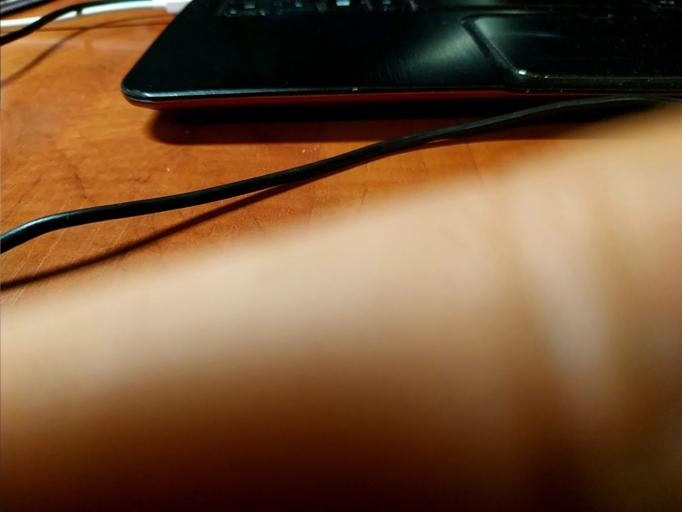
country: RU
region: Tverskaya
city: Spirovo
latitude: 57.3627
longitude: 34.9542
